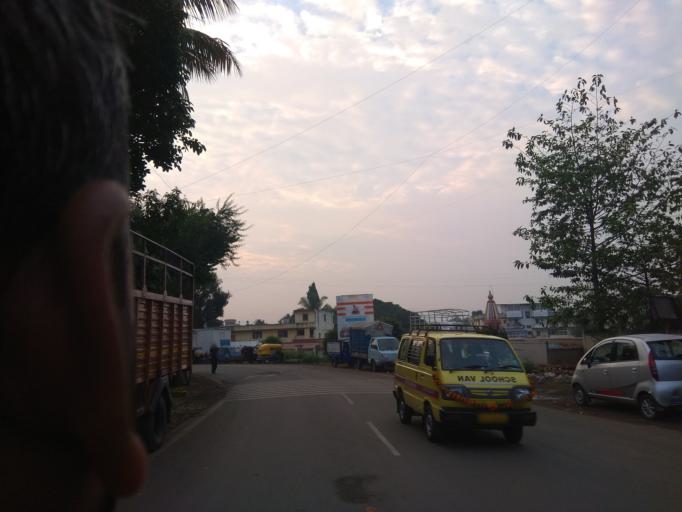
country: IN
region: Maharashtra
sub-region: Pune Division
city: Kharakvasla
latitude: 18.4820
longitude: 73.8054
